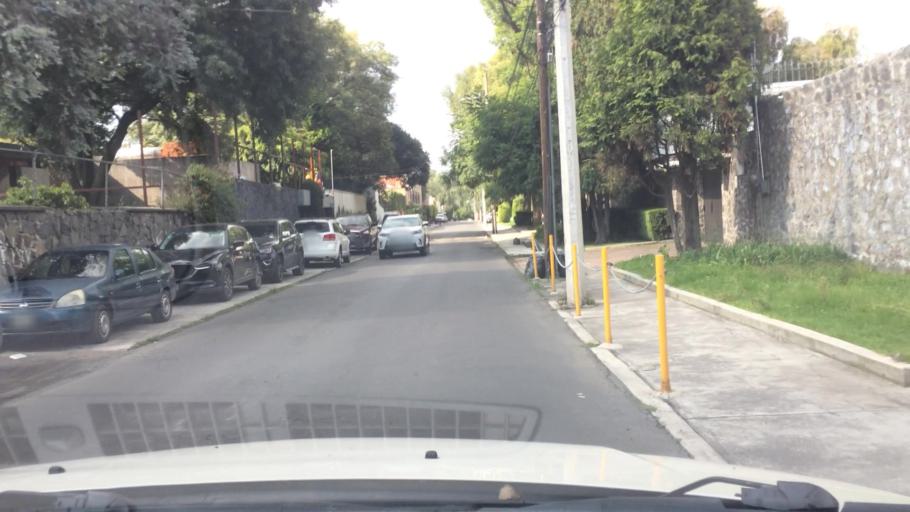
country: MX
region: Mexico City
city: Magdalena Contreras
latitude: 19.3120
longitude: -99.2139
